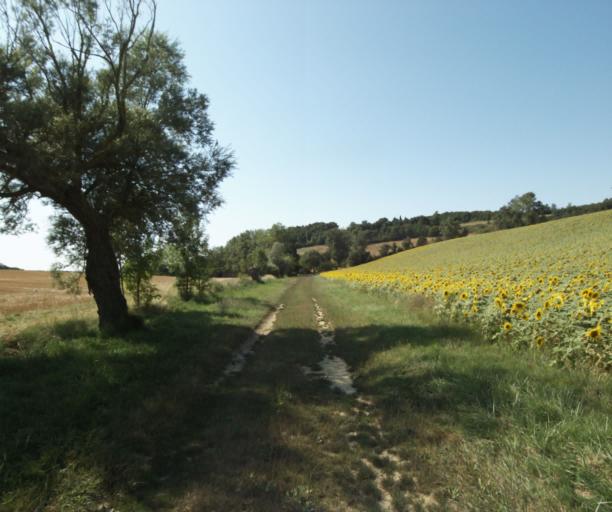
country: FR
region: Midi-Pyrenees
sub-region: Departement de la Haute-Garonne
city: Saint-Felix-Lauragais
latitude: 43.4357
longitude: 1.8489
